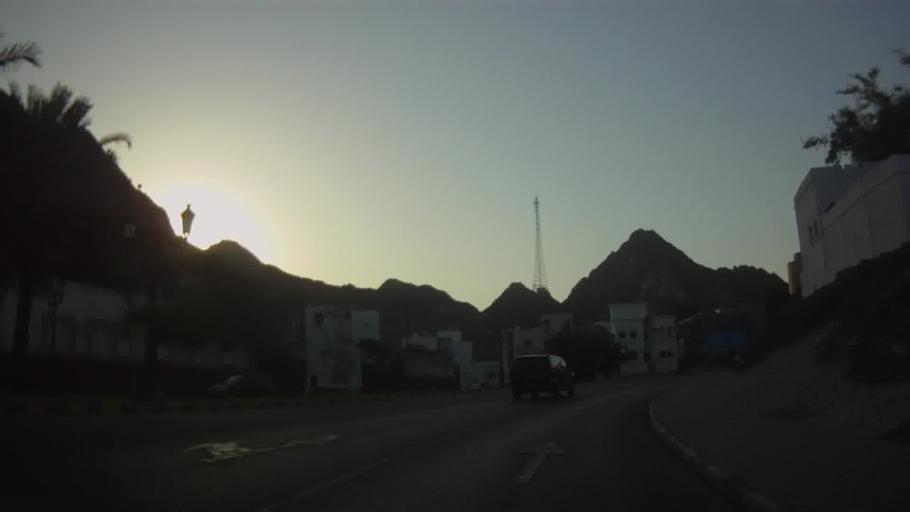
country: OM
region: Muhafazat Masqat
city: Muscat
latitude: 23.6167
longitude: 58.5880
